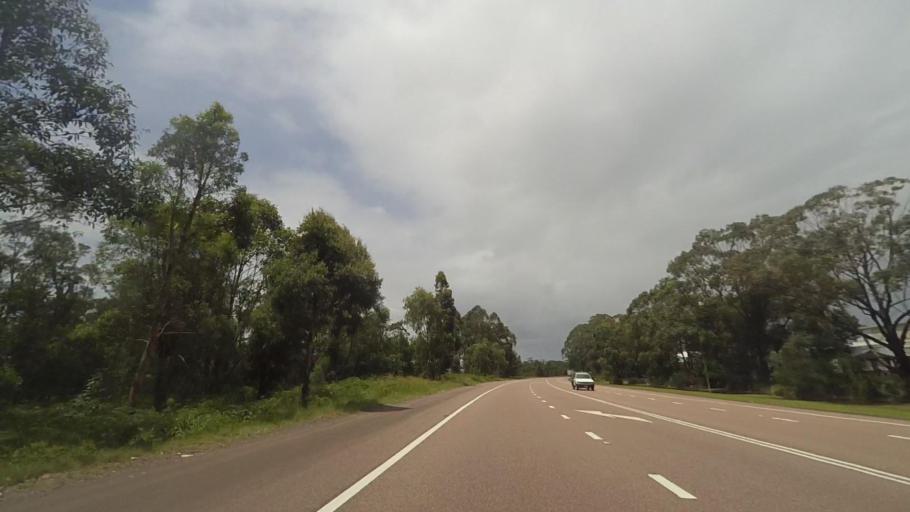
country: AU
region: New South Wales
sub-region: Wyong Shire
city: Chittaway Bay
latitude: -33.3307
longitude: 151.4040
